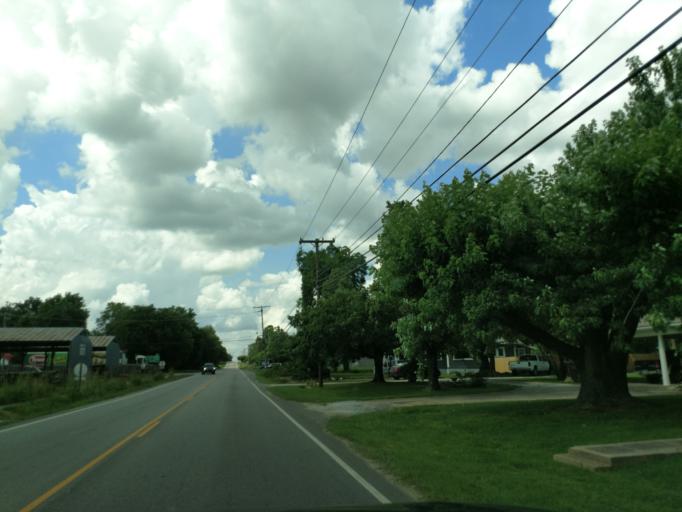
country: US
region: Arkansas
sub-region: Carroll County
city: Berryville
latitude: 36.3726
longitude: -93.5672
